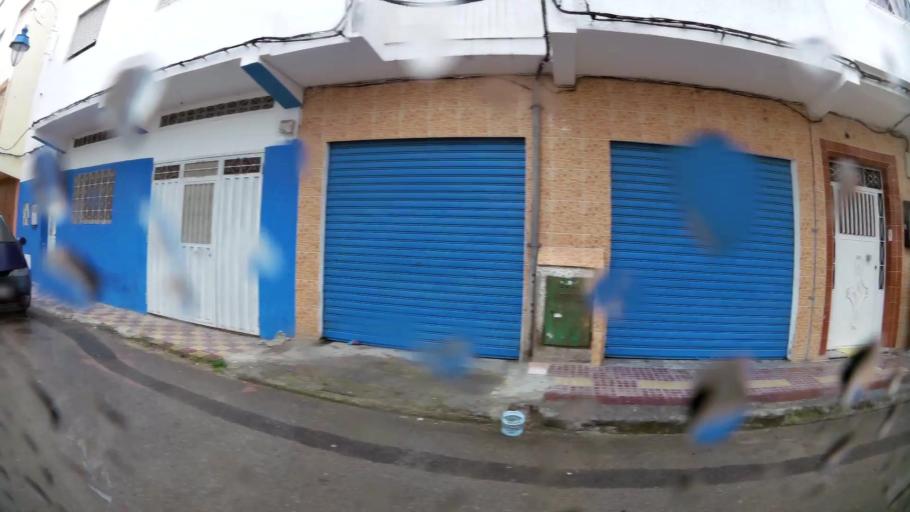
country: MA
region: Tanger-Tetouan
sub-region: Tetouan
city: Martil
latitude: 35.6144
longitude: -5.2836
